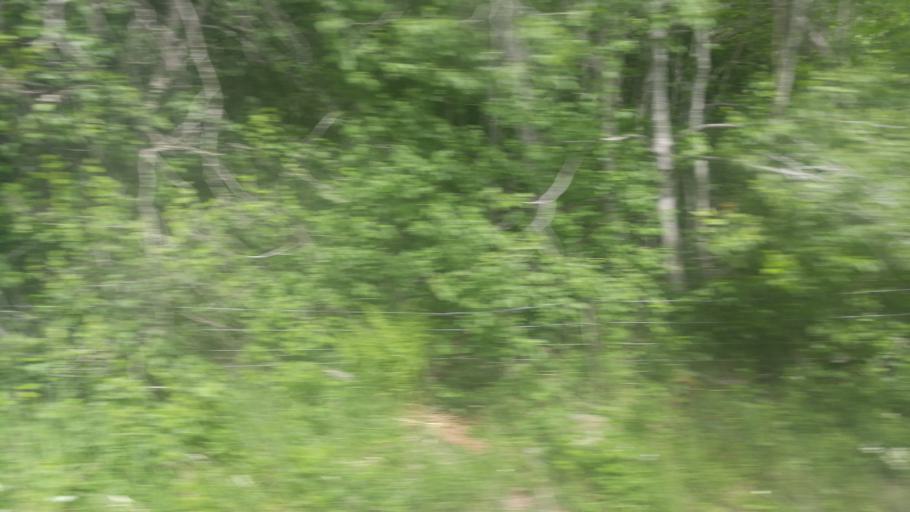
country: NO
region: Sor-Trondelag
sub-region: Selbu
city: Mebonden
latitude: 62.9563
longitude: 10.7886
